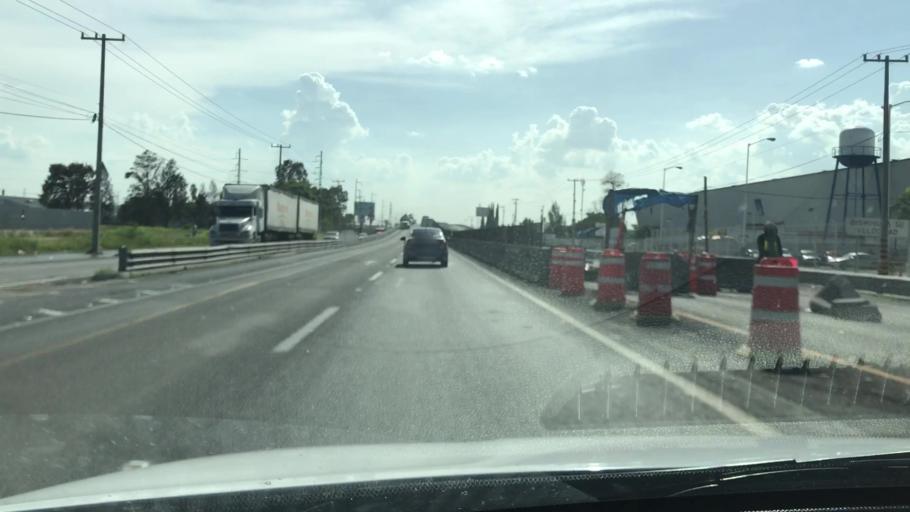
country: MX
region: Guanajuato
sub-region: Celaya
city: Colonia Fraccionamiento el Puente
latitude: 20.5155
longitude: -100.8900
